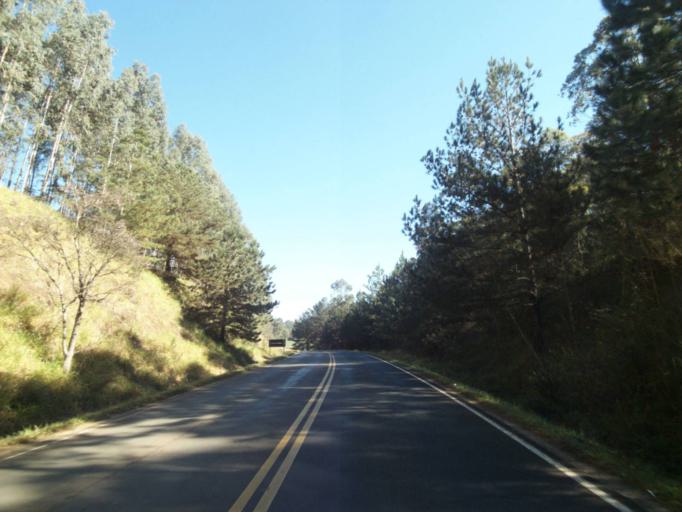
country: BR
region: Parana
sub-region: Tibagi
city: Tibagi
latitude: -24.5000
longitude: -50.4500
